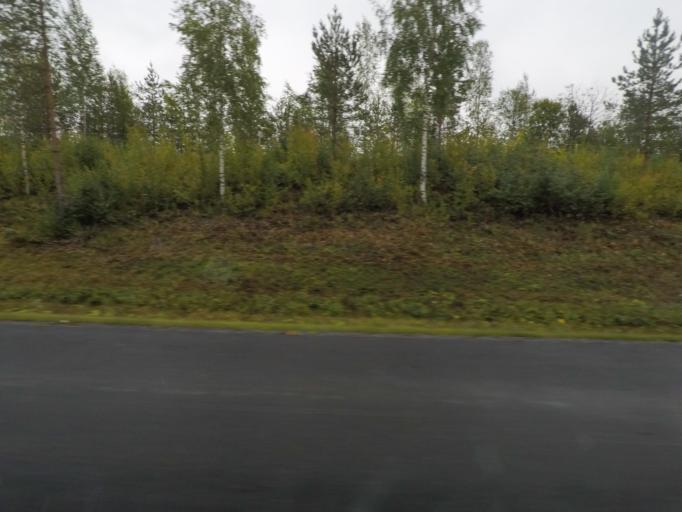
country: FI
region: Northern Savo
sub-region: Kuopio
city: Kuopio
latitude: 62.8075
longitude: 27.6016
